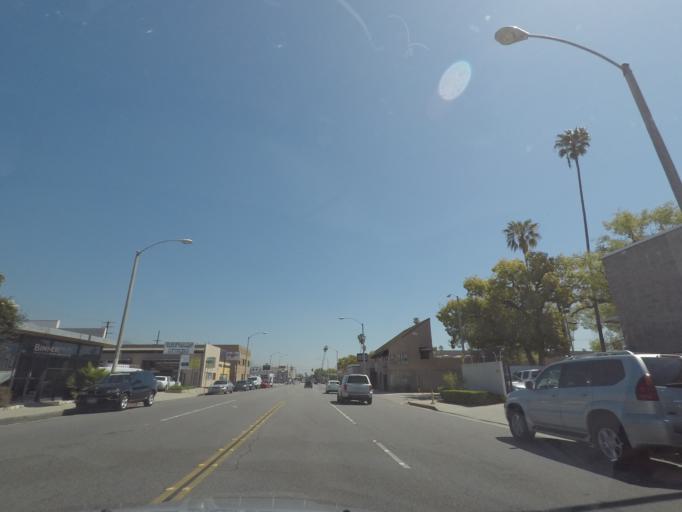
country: US
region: California
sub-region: Los Angeles County
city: East Pasadena
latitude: 34.1495
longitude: -118.1189
